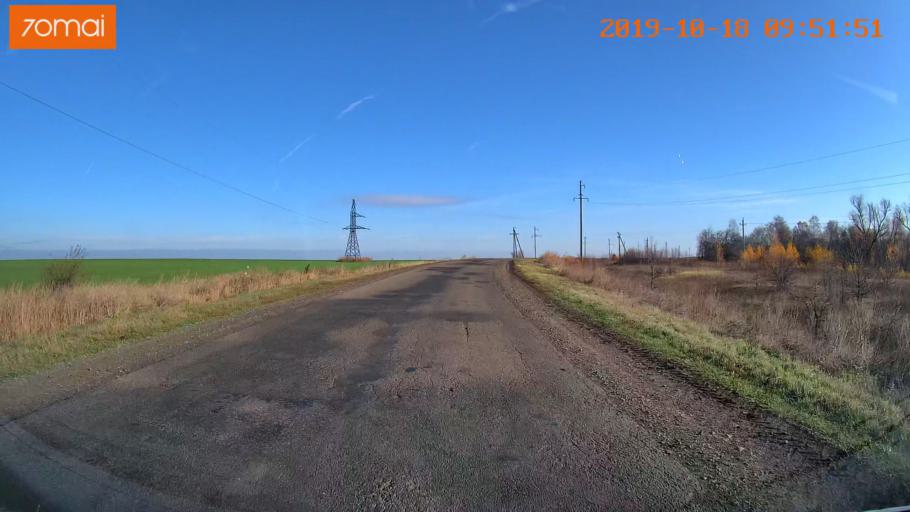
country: RU
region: Tula
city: Kazachka
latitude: 53.3457
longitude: 38.2991
